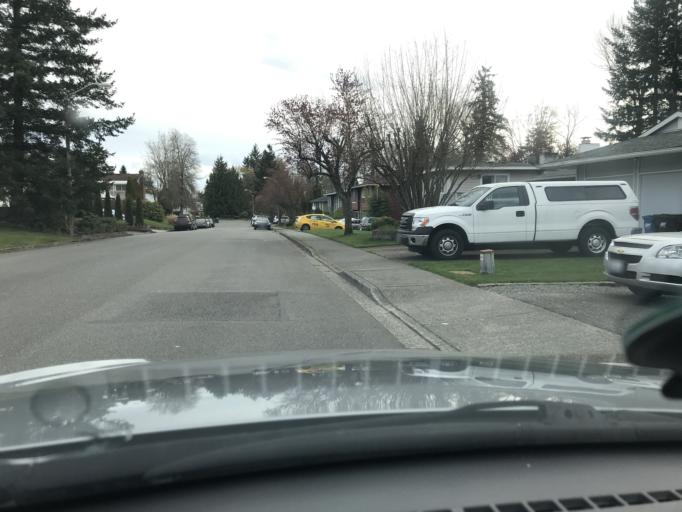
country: US
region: Washington
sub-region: King County
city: East Hill-Meridian
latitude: 47.4129
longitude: -122.1753
